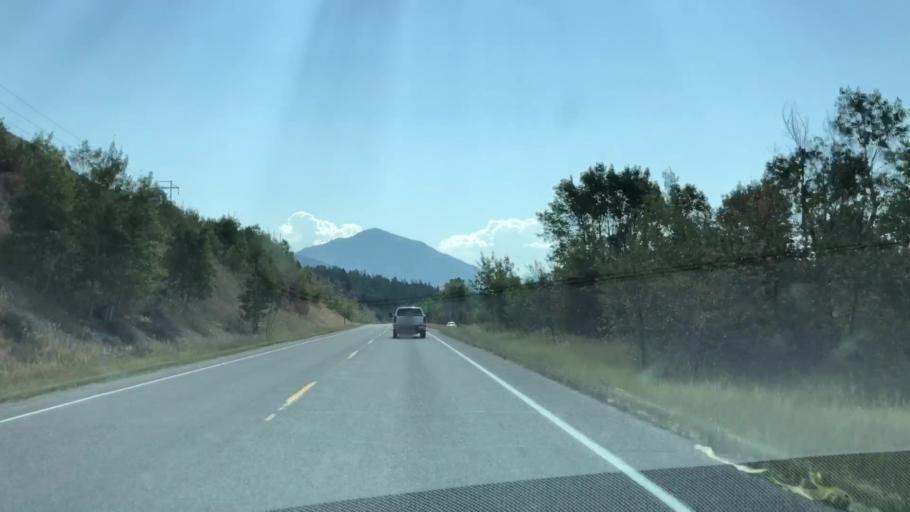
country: US
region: Wyoming
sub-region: Teton County
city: Hoback
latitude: 43.2064
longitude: -111.0526
